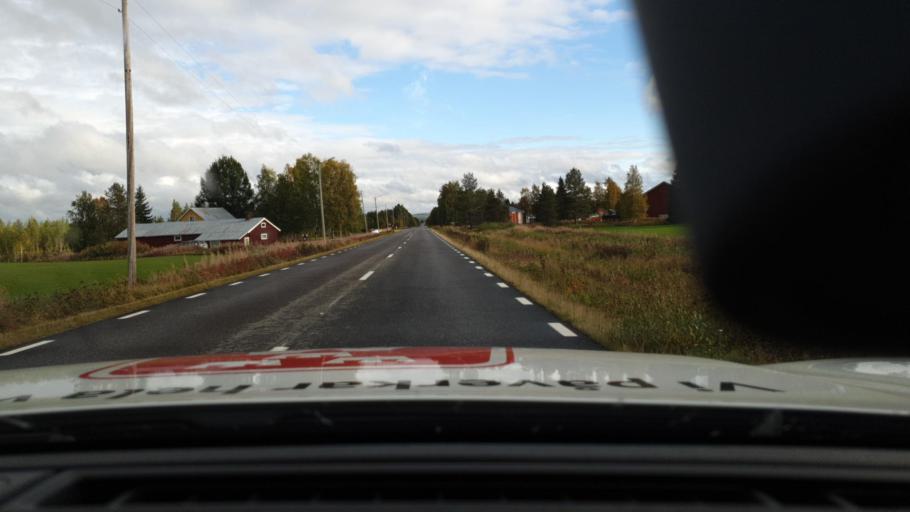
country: SE
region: Norrbotten
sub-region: Overkalix Kommun
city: OEverkalix
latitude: 66.9536
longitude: 22.7038
